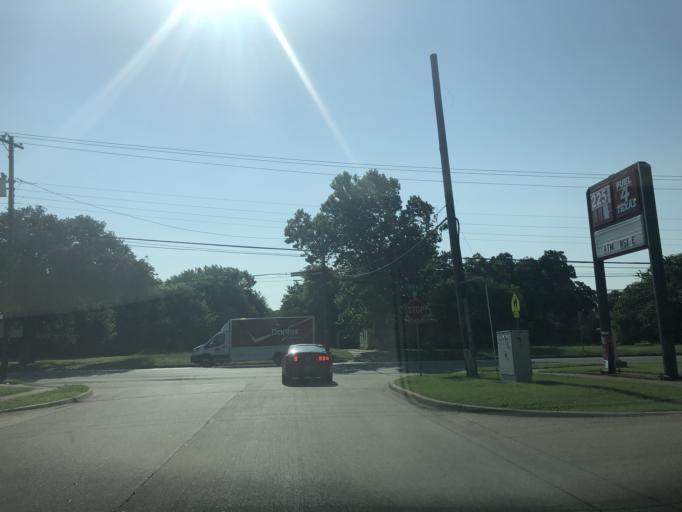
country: US
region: Texas
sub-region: Dallas County
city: Irving
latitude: 32.8106
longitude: -96.9769
